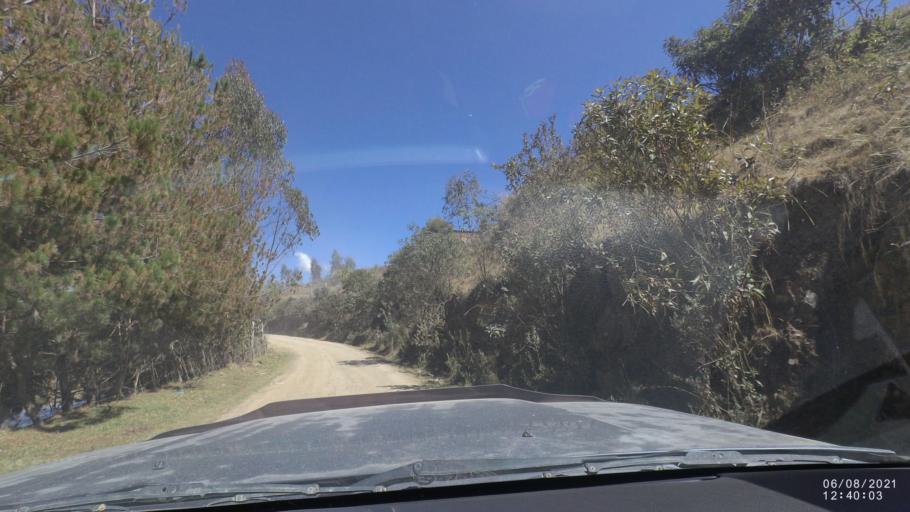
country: BO
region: Cochabamba
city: Colchani
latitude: -16.7820
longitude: -66.6633
